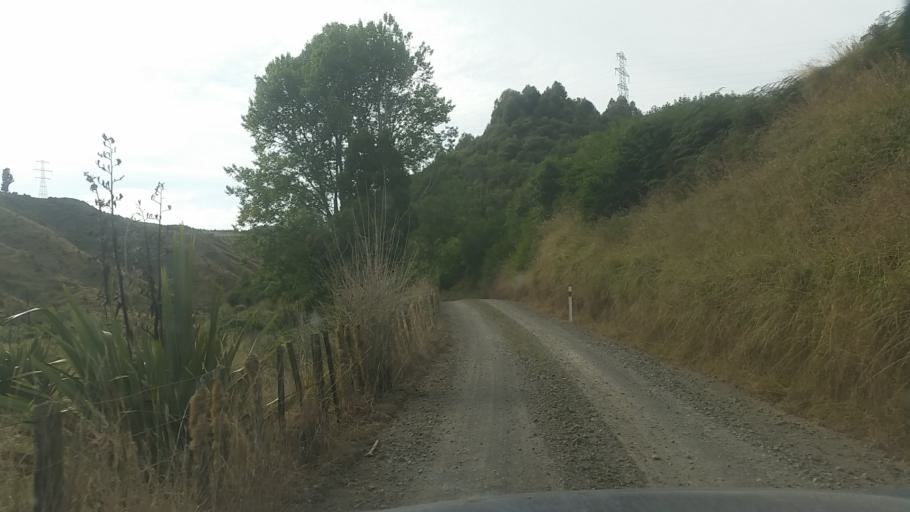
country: NZ
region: Taranaki
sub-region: New Plymouth District
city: Waitara
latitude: -39.1346
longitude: 174.7068
